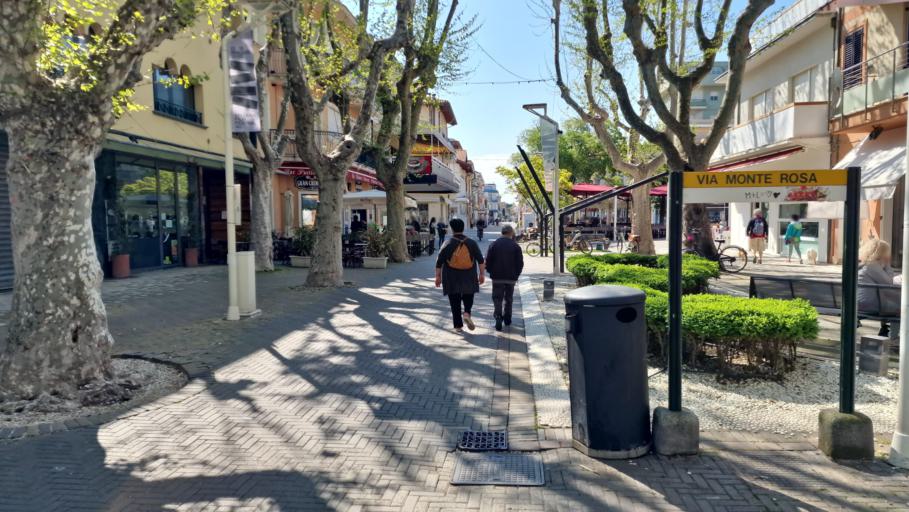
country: IT
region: Emilia-Romagna
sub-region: Provincia di Rimini
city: Bellaria-Igea Marina
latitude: 44.1468
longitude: 12.4633
